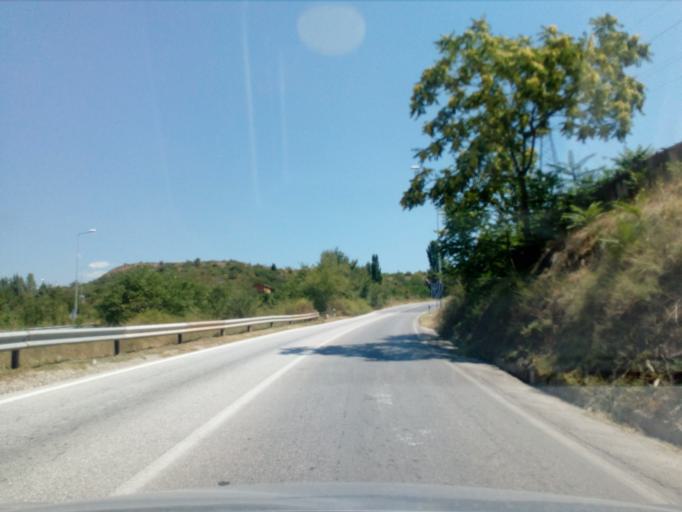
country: MK
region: Veles
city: Veles
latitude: 41.7264
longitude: 21.7878
